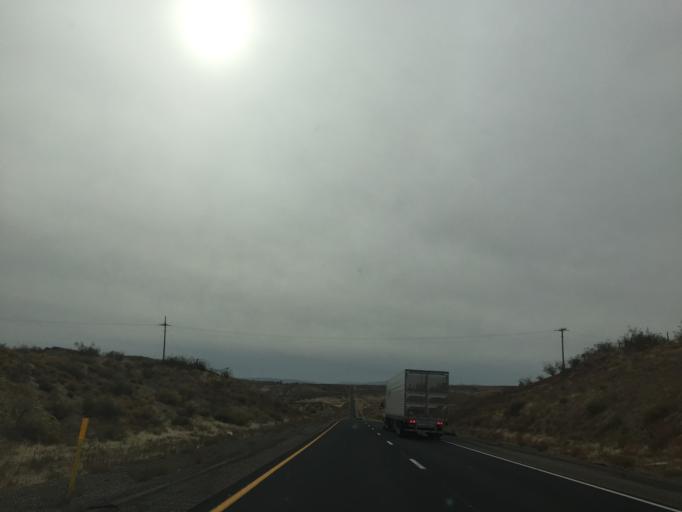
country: US
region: Utah
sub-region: Washington County
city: Hurricane
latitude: 37.2121
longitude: -113.3924
